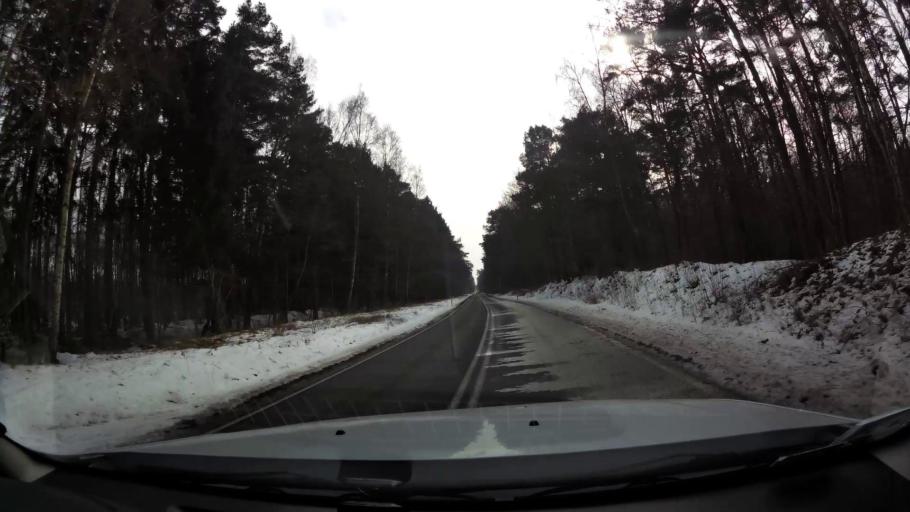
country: PL
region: West Pomeranian Voivodeship
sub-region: Powiat kamienski
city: Dziwnow
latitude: 53.9885
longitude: 14.6298
